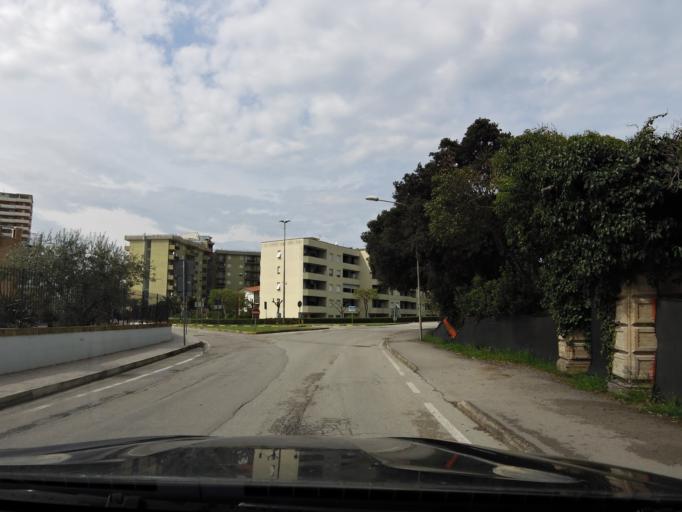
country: IT
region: The Marches
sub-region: Provincia di Macerata
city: Porto Recanati
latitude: 43.4208
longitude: 13.6700
